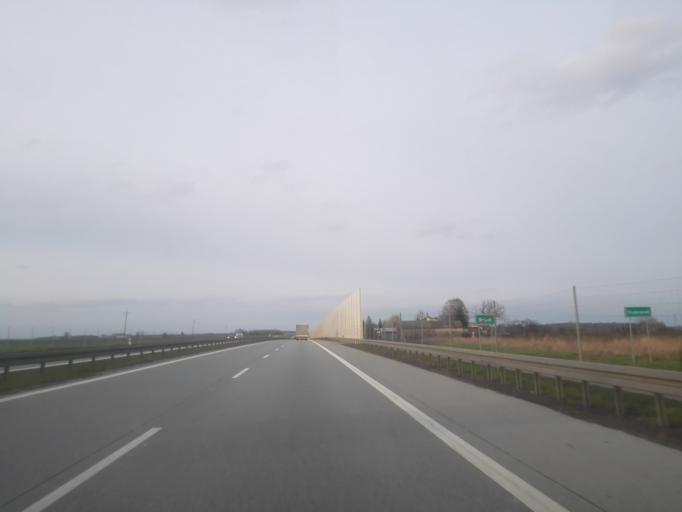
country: PL
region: Lodz Voivodeship
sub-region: Powiat skierniewicki
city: Kowiesy
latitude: 51.8492
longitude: 20.3679
